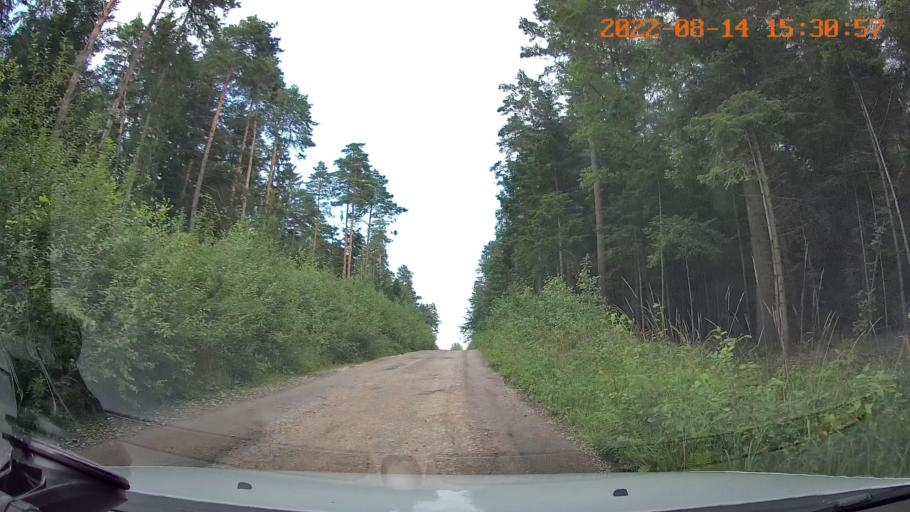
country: PL
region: Swietokrzyskie
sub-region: Powiat kielecki
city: Zagnansk
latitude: 50.9672
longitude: 20.6609
